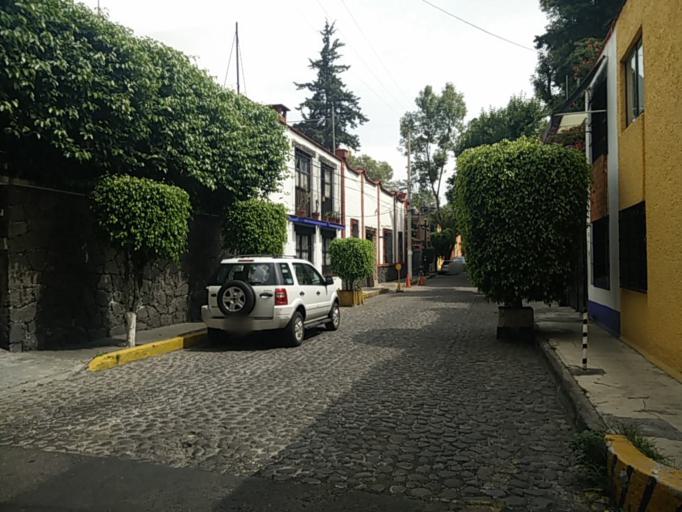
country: MX
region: Mexico City
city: Coyoacan
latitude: 19.3458
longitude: -99.1629
